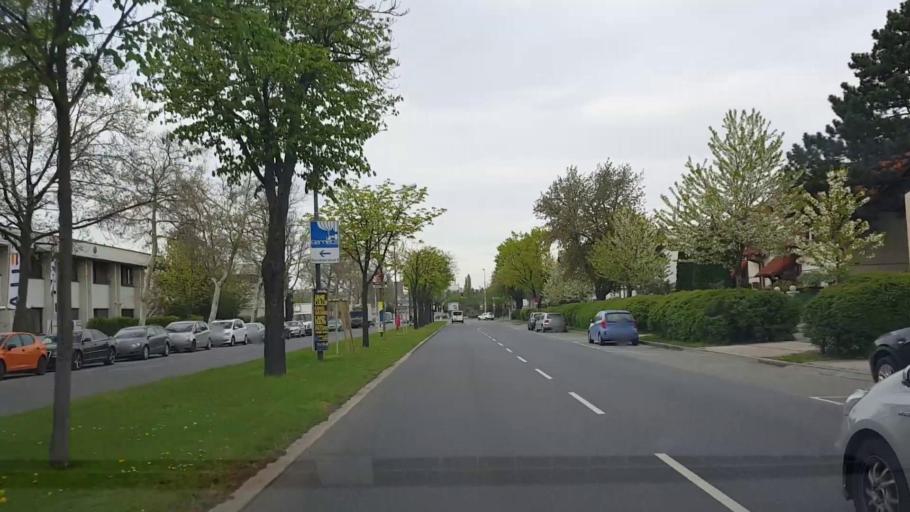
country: AT
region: Lower Austria
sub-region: Politischer Bezirk Modling
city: Vosendorf
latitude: 48.1430
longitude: 16.3604
